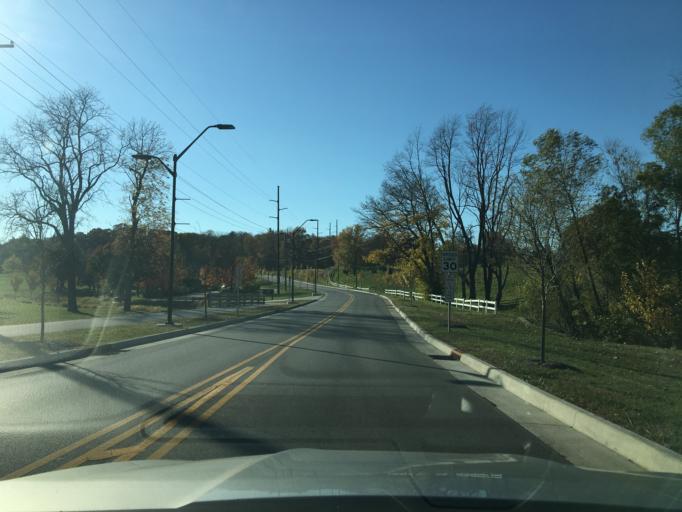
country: US
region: Indiana
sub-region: Tippecanoe County
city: West Lafayette
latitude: 40.4315
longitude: -86.9283
